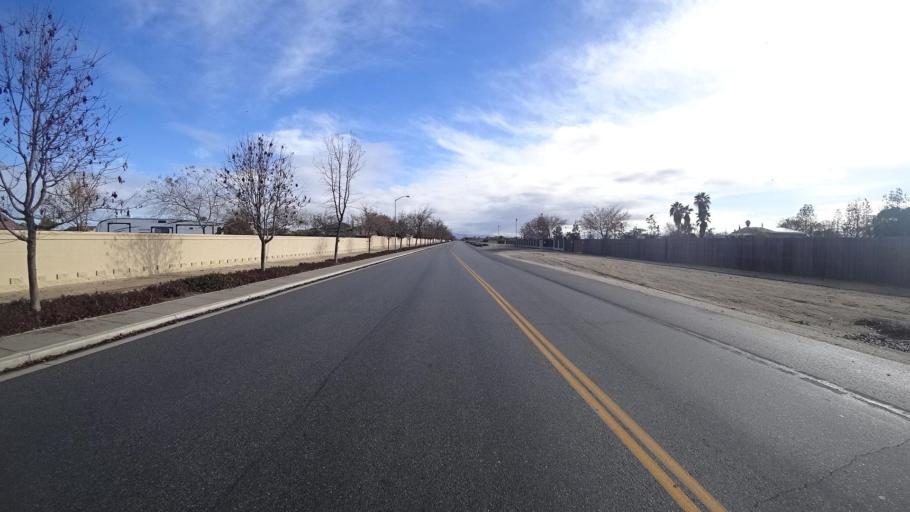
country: US
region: California
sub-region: Kern County
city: Rosedale
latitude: 35.3908
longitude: -119.1800
